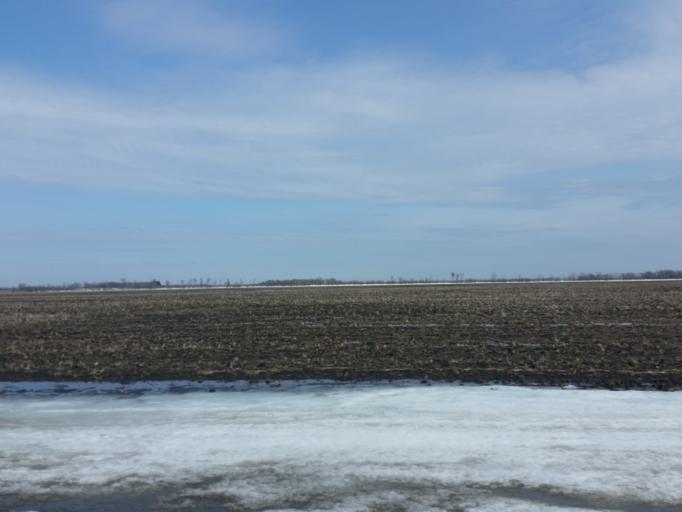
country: US
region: North Dakota
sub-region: Walsh County
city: Grafton
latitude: 48.4217
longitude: -97.2558
